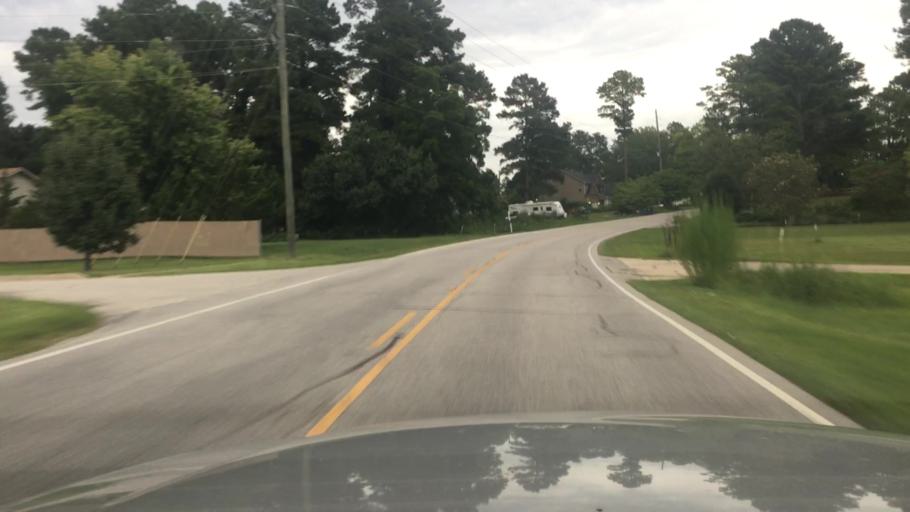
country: US
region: North Carolina
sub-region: Hoke County
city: Rockfish
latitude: 34.9817
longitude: -79.0468
